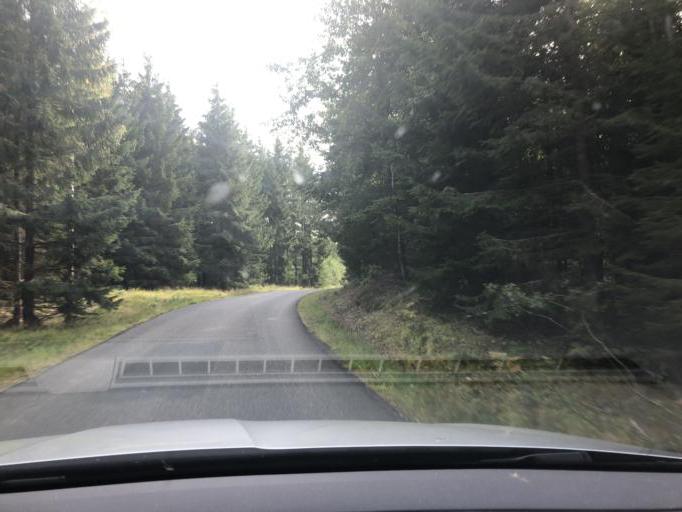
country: SE
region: Joenkoeping
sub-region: Vetlanda Kommun
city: Ekenassjon
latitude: 57.4972
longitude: 14.9048
